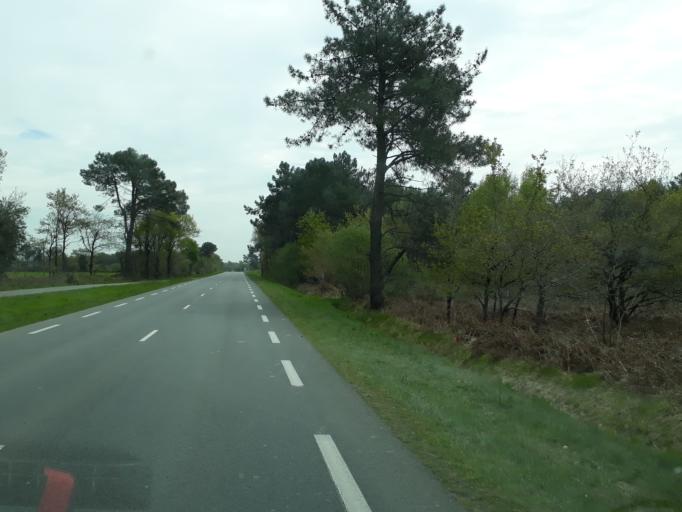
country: FR
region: Brittany
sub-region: Departement du Morbihan
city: Peaule
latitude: 47.5298
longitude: -2.3880
